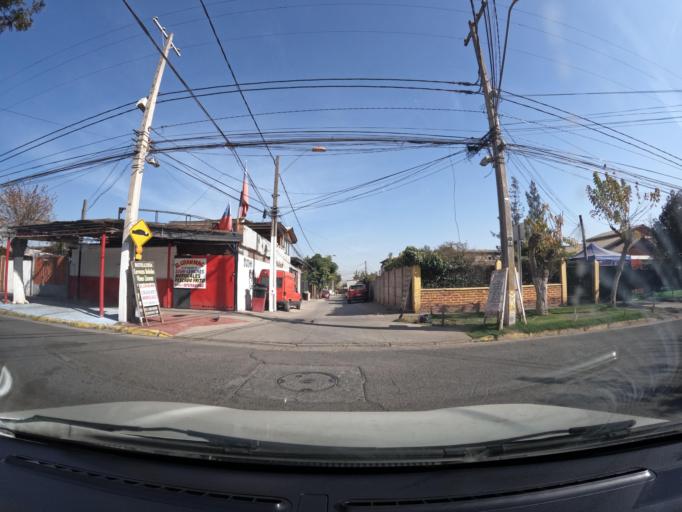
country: CL
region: Santiago Metropolitan
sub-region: Provincia de Santiago
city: Villa Presidente Frei, Nunoa, Santiago, Chile
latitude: -33.4694
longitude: -70.5558
